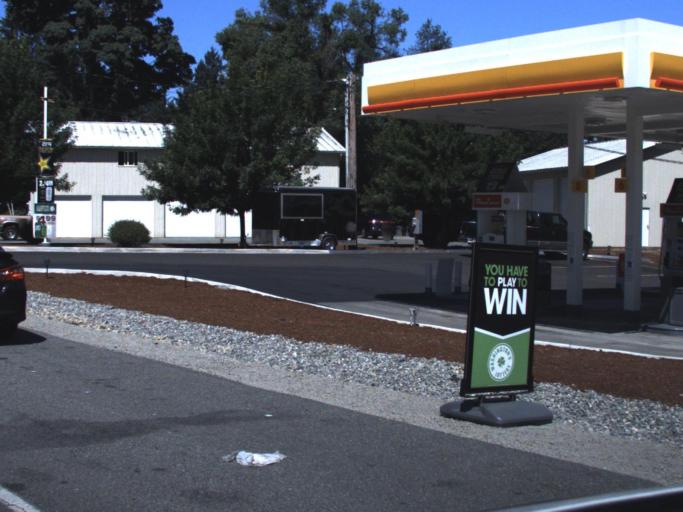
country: US
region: Washington
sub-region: King County
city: East Renton Highlands
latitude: 47.5006
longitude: -122.1231
